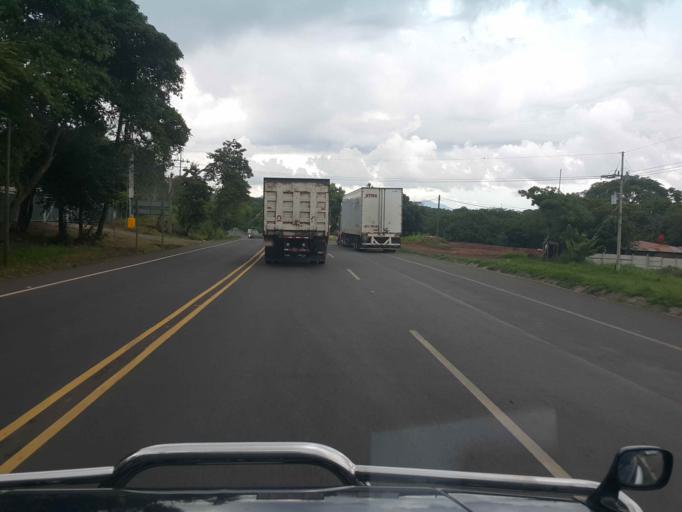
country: CR
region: Puntarenas
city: Esparza
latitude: 9.8941
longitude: -84.6520
